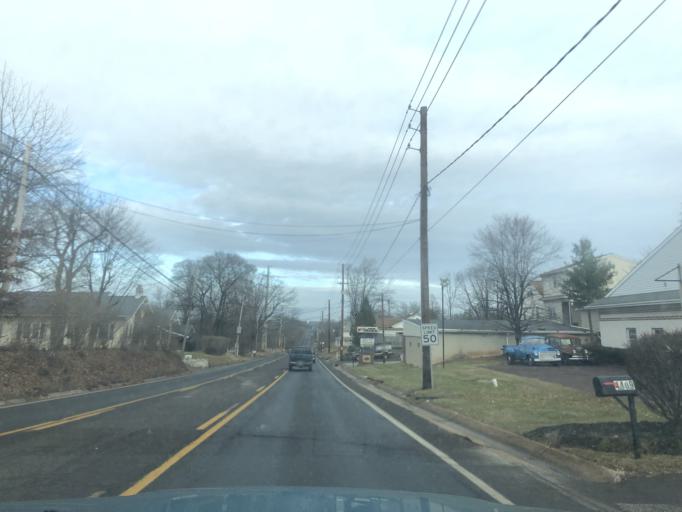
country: US
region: Pennsylvania
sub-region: Bucks County
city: Sellersville
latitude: 40.3313
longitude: -75.3033
